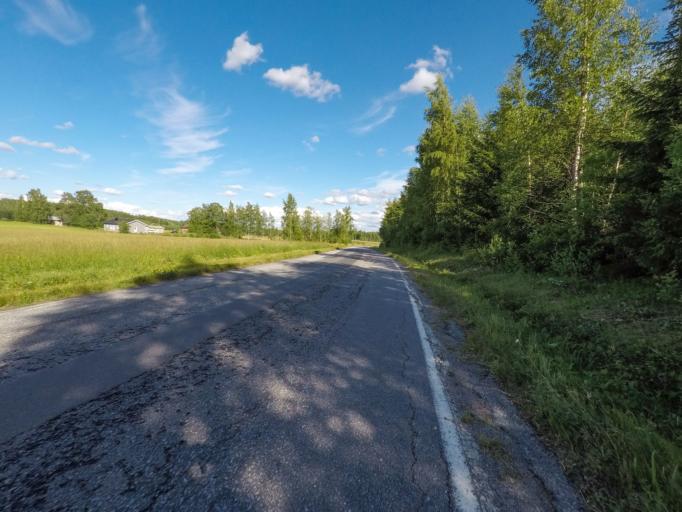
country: FI
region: South Karelia
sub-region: Imatra
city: Imatra
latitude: 61.1405
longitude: 28.6419
